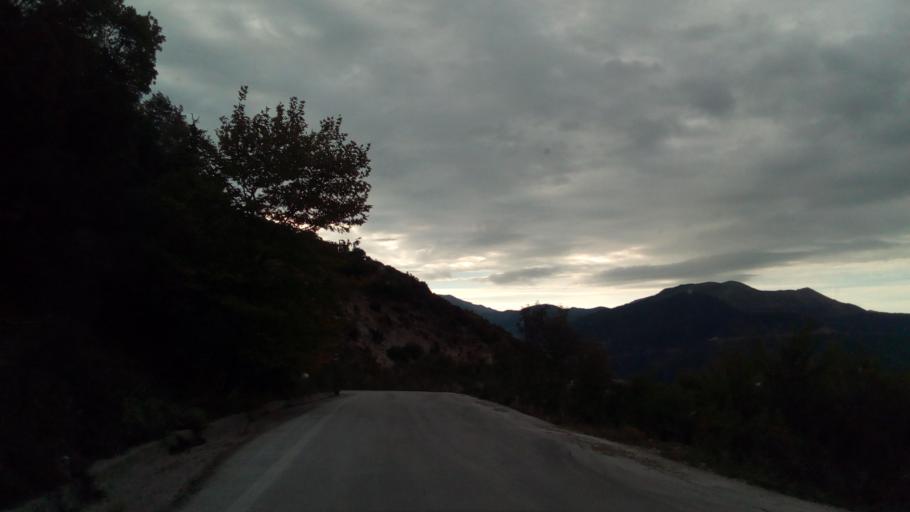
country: GR
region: West Greece
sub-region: Nomos Aitolias kai Akarnanias
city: Thermo
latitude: 38.6052
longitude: 21.8016
